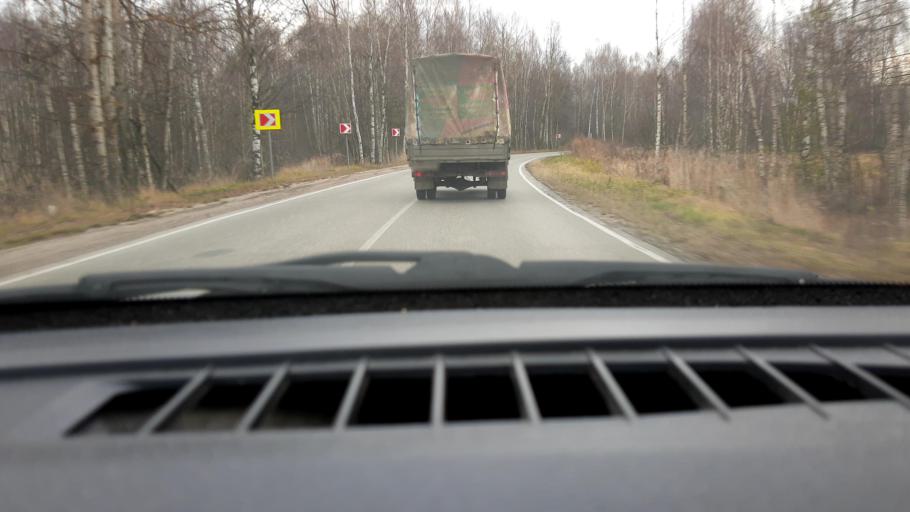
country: RU
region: Nizjnij Novgorod
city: Neklyudovo
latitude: 56.4983
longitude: 43.8530
